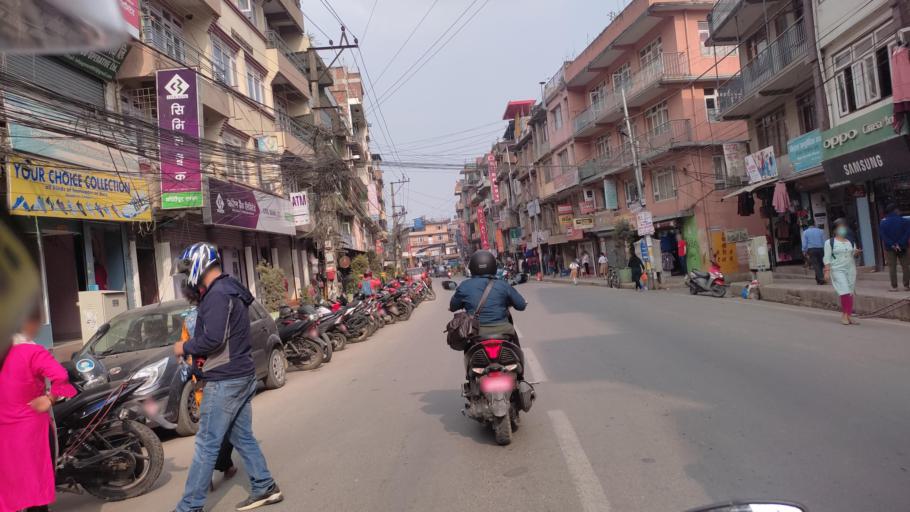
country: NP
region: Central Region
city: Kirtipur
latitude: 27.6748
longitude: 85.2780
